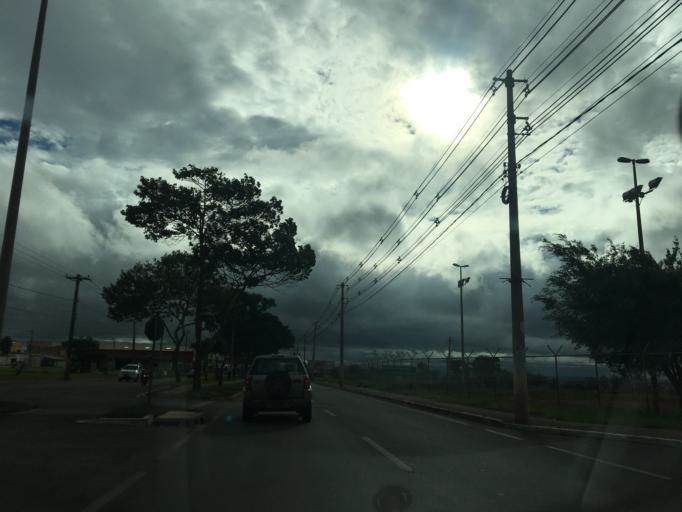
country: BR
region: Goias
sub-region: Luziania
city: Luziania
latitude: -16.0175
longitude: -48.0187
